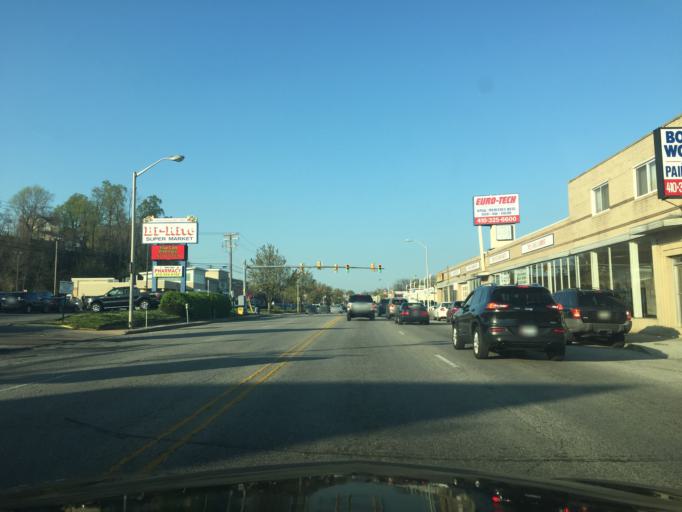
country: US
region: Maryland
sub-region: Baltimore County
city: Overlea
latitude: 39.3462
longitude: -76.5404
